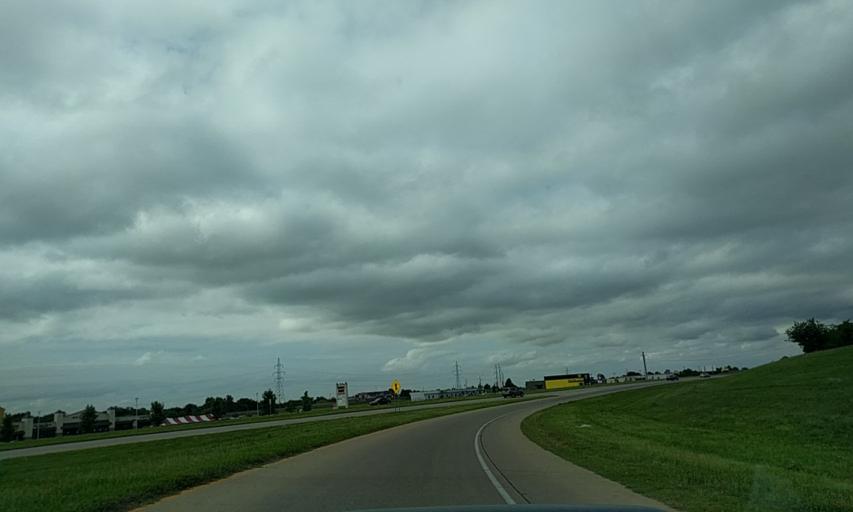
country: US
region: Oklahoma
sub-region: Tulsa County
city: Owasso
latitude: 36.2919
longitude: -95.8374
